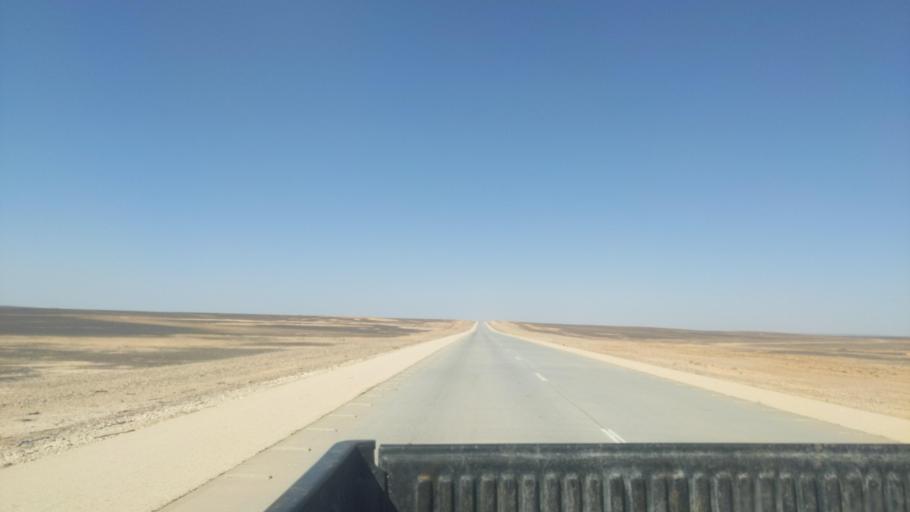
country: JO
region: Amman
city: Al Azraq ash Shamali
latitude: 31.4396
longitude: 36.7517
